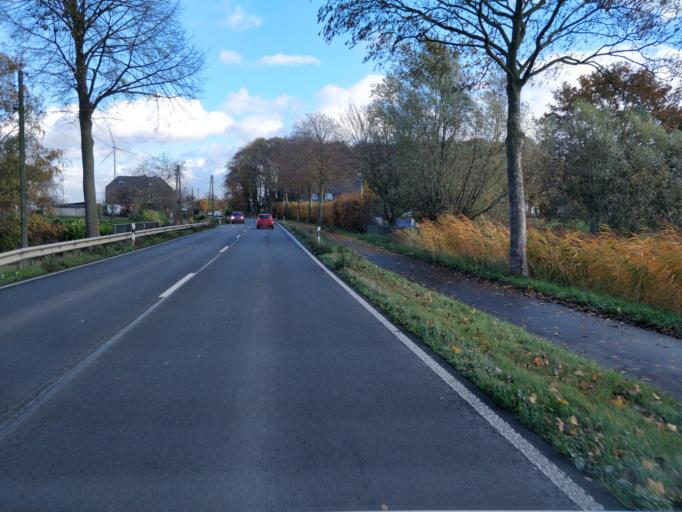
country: DE
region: North Rhine-Westphalia
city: Rees
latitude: 51.7762
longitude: 6.4328
